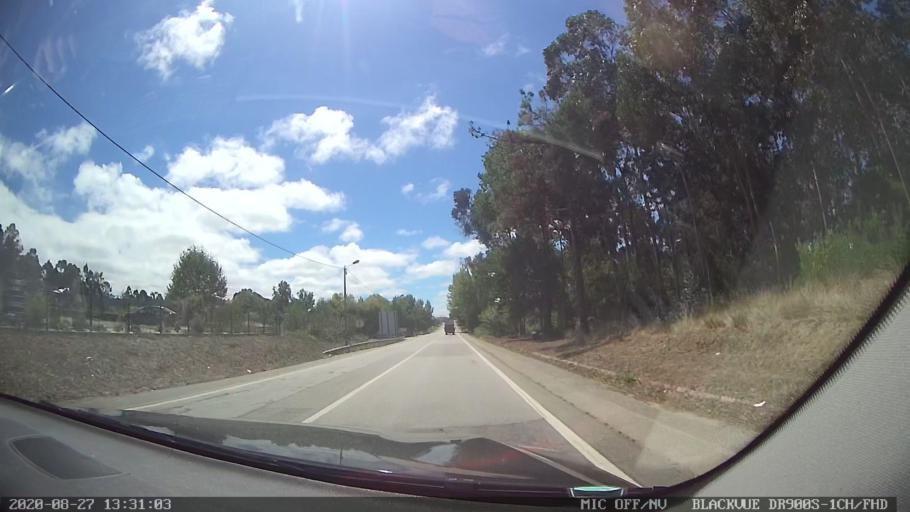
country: PT
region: Aveiro
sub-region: Vagos
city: Vagos
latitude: 40.5009
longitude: -8.6815
